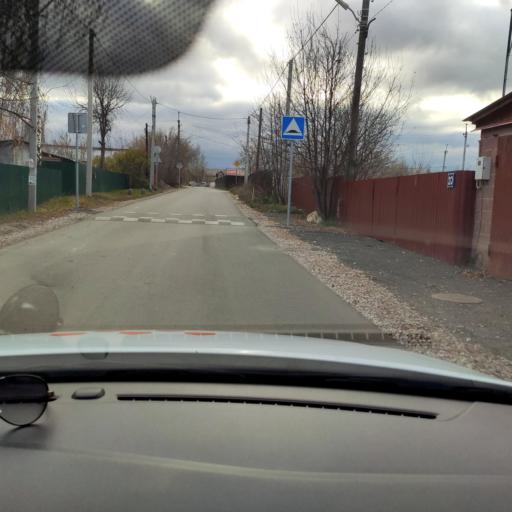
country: RU
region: Tatarstan
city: Stolbishchi
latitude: 55.7388
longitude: 49.2698
